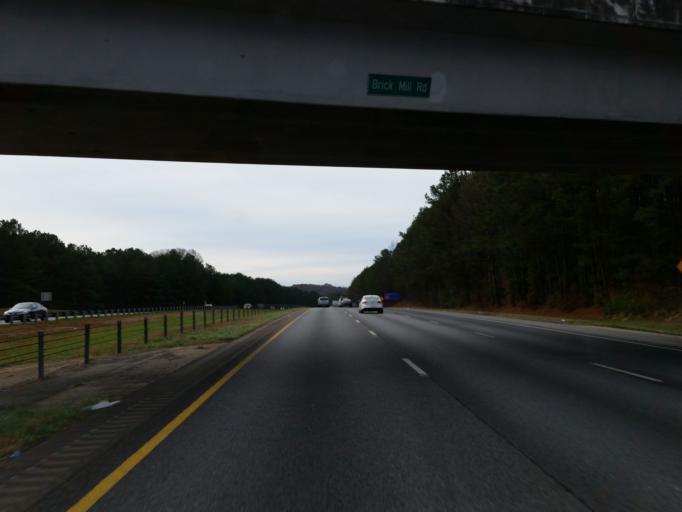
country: US
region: Georgia
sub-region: Cherokee County
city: Canton
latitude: 34.2113
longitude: -84.4920
